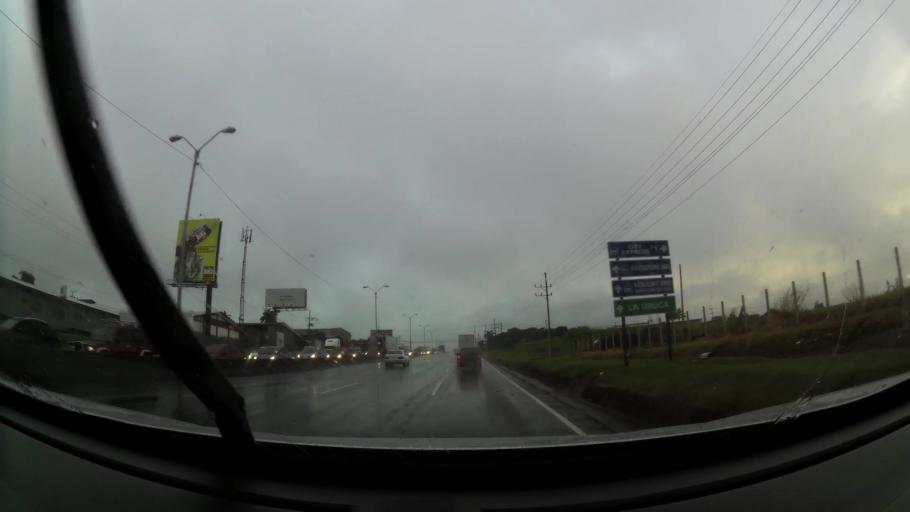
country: CR
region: Heredia
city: La Asuncion
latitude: 9.9854
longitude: -84.1641
